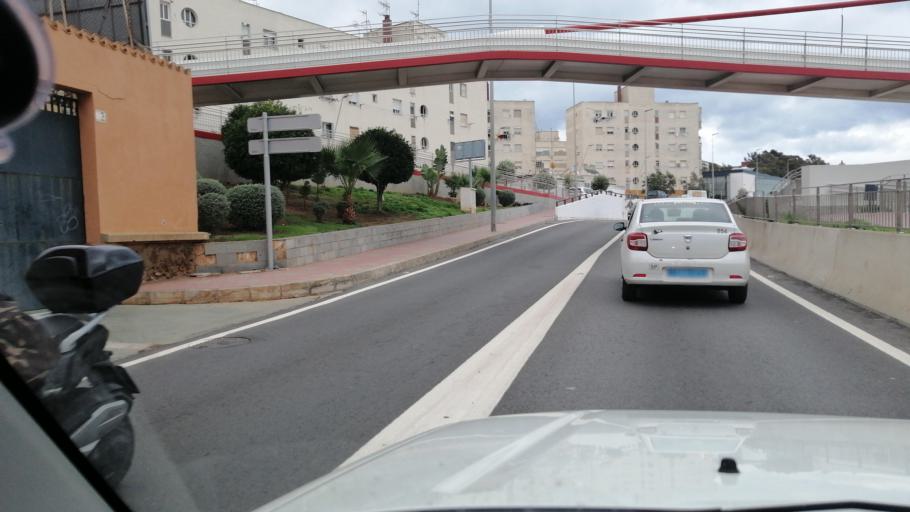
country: ES
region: Ceuta
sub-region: Ceuta
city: Ceuta
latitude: 35.8800
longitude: -5.3343
